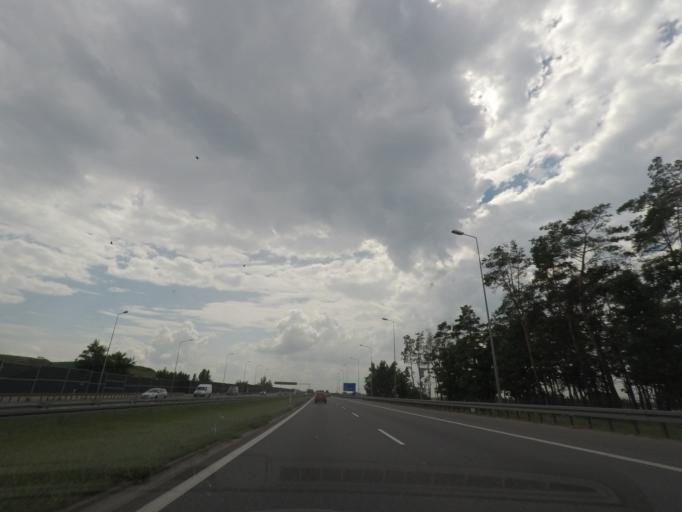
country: PL
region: Masovian Voivodeship
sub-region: Powiat warszawski zachodni
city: Ozarow Mazowiecki
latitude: 52.1838
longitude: 20.7734
